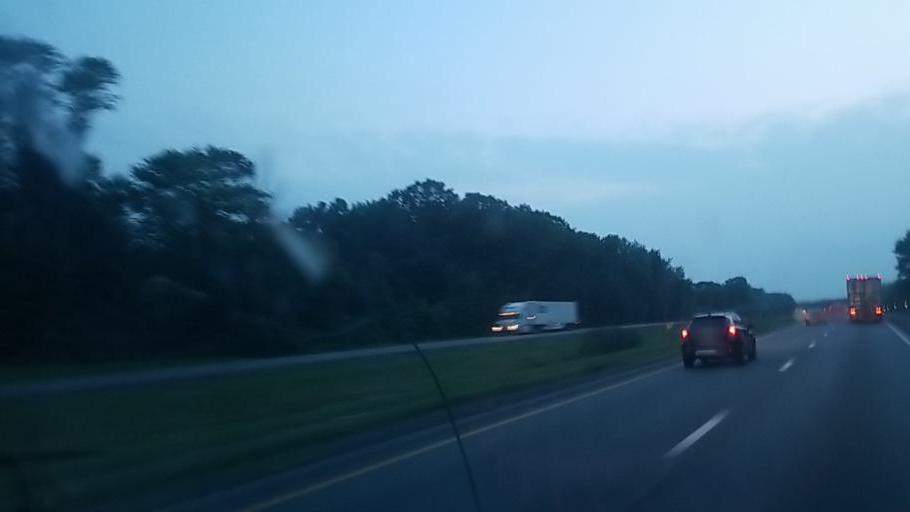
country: US
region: New York
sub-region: Madison County
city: Bolivar
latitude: 43.0956
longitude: -75.8677
